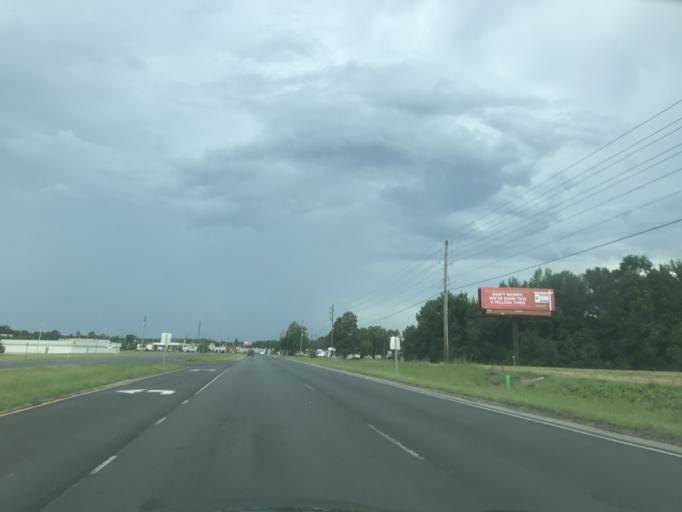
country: US
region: North Carolina
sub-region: Johnston County
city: Clayton
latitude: 35.6175
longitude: -78.4198
